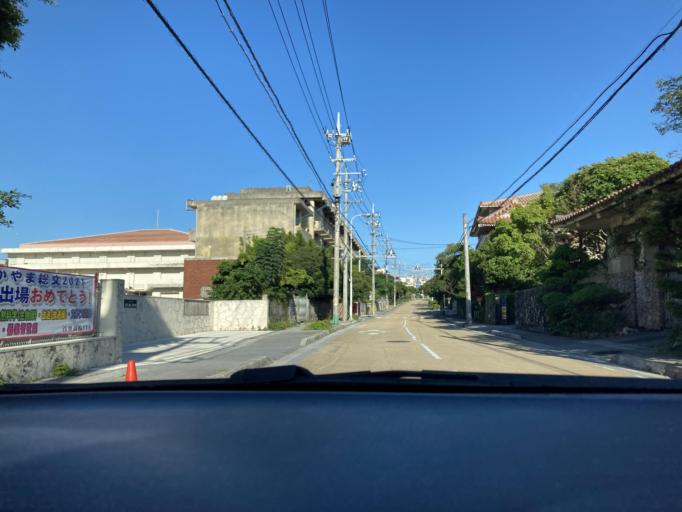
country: JP
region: Okinawa
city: Naha-shi
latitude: 26.2190
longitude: 127.7129
